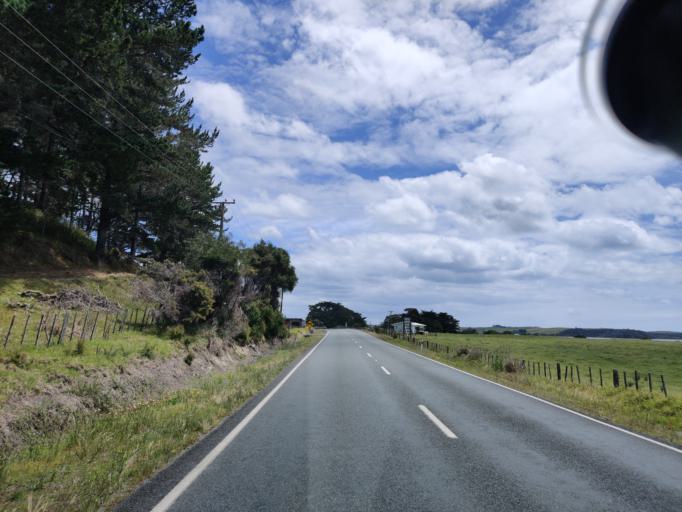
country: NZ
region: Northland
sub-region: Far North District
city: Kaitaia
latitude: -34.7987
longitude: 173.1086
